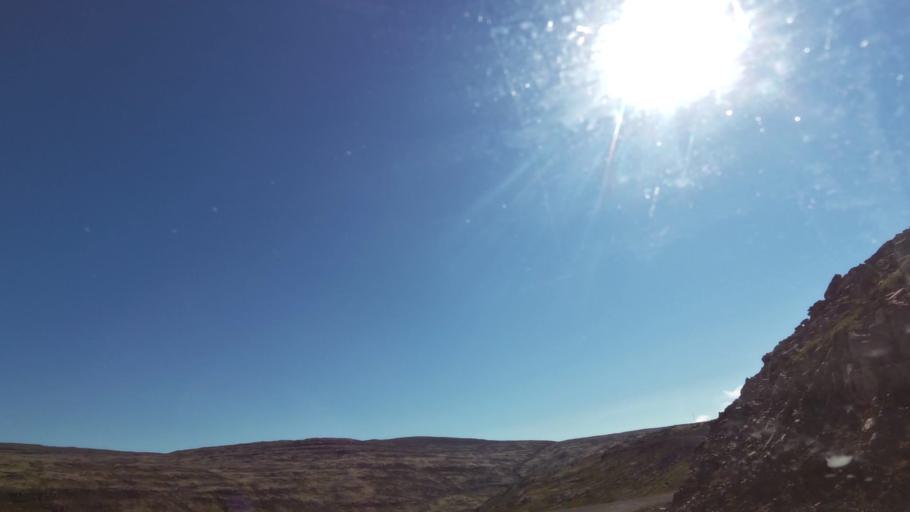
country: IS
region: West
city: Olafsvik
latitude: 65.5552
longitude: -24.1970
